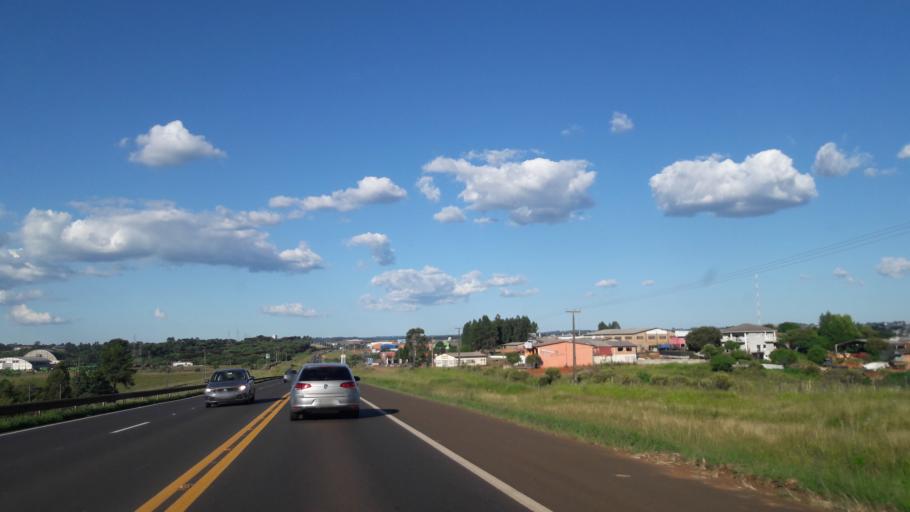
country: BR
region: Parana
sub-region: Guarapuava
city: Guarapuava
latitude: -25.3789
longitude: -51.5072
